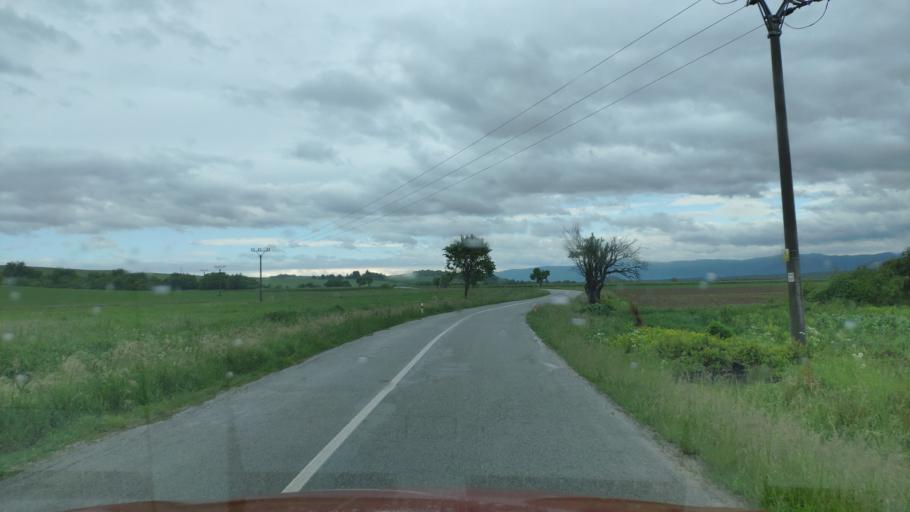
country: SK
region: Kosicky
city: Moldava nad Bodvou
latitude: 48.5380
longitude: 21.0638
